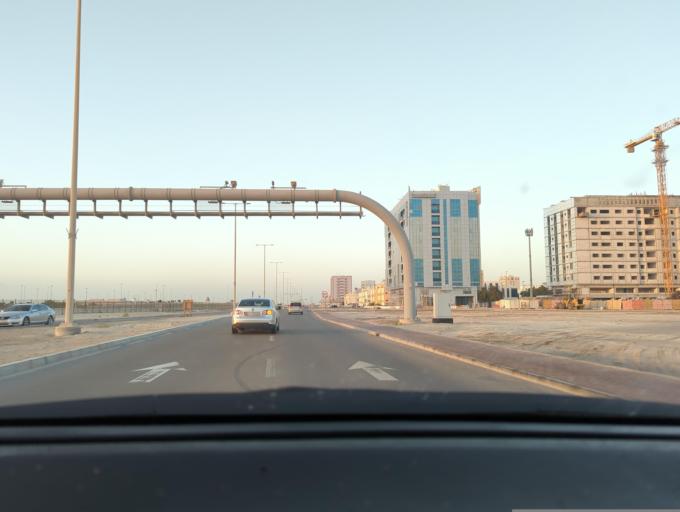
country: AE
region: Abu Dhabi
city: Abu Dhabi
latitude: 24.3157
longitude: 54.5305
